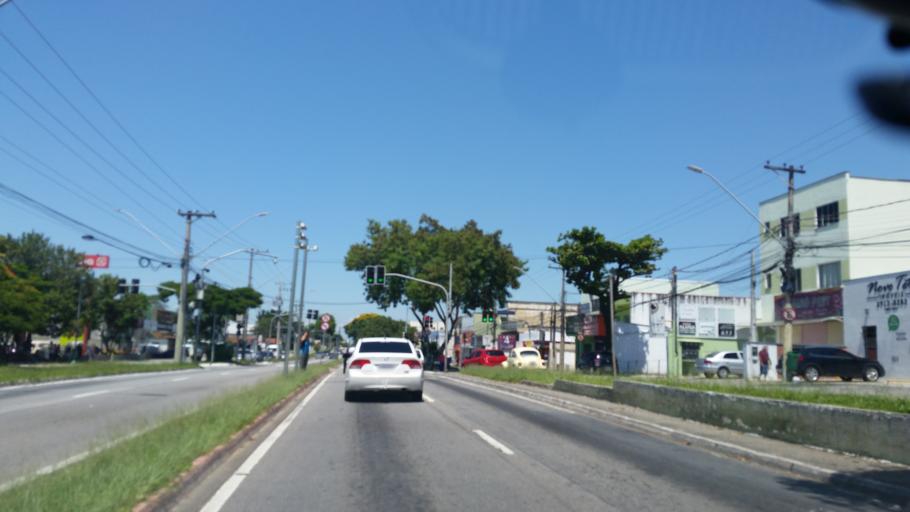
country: BR
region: Sao Paulo
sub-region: Sao Jose Dos Campos
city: Sao Jose dos Campos
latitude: -23.1749
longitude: -45.8210
